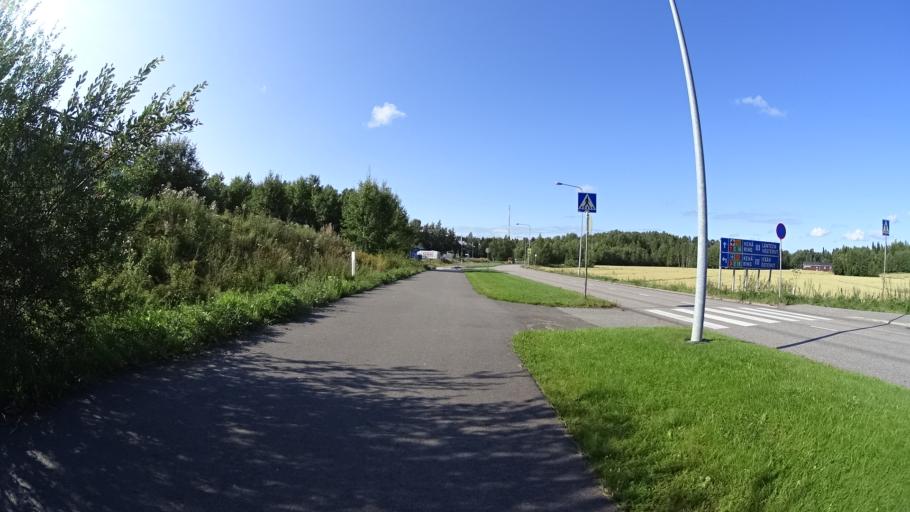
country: FI
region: Uusimaa
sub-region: Helsinki
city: Kauniainen
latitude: 60.2653
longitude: 24.7307
